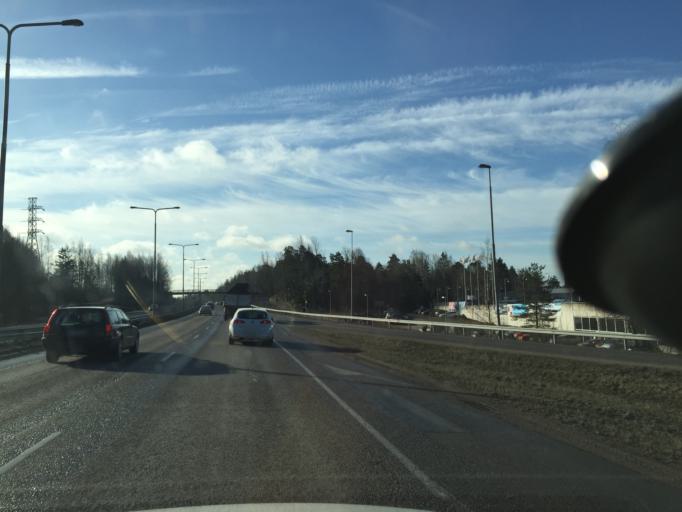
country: FI
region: Uusimaa
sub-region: Helsinki
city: Teekkarikylae
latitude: 60.2622
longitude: 24.8759
